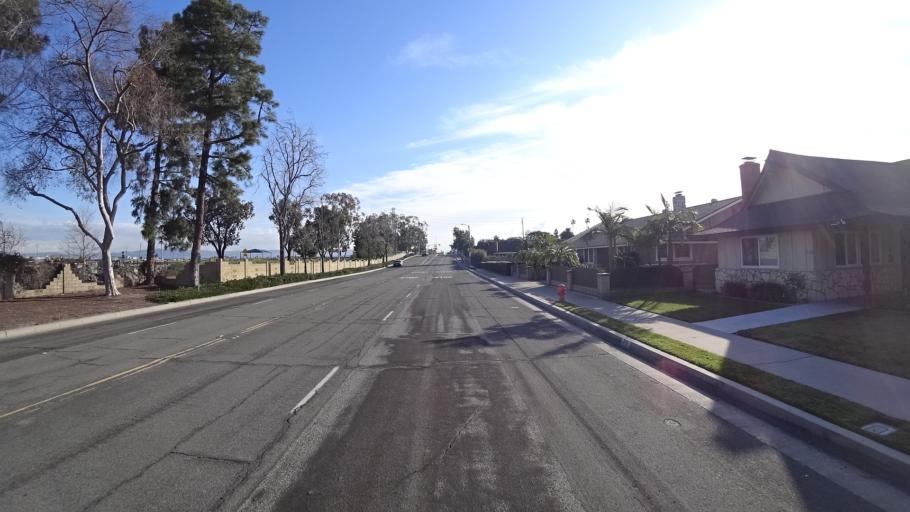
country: US
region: California
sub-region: Orange County
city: Placentia
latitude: 33.8455
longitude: -117.8457
